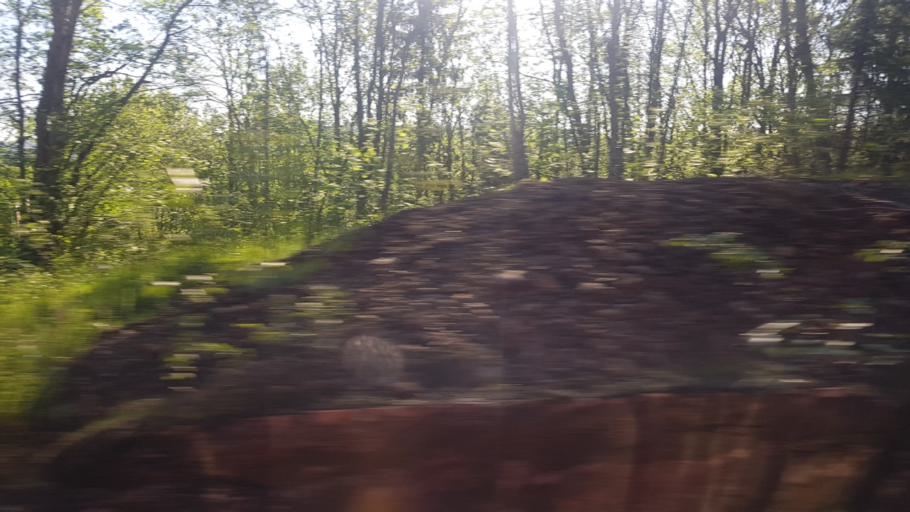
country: NO
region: Sor-Trondelag
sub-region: Trondheim
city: Trondheim
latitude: 63.3790
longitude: 10.3672
